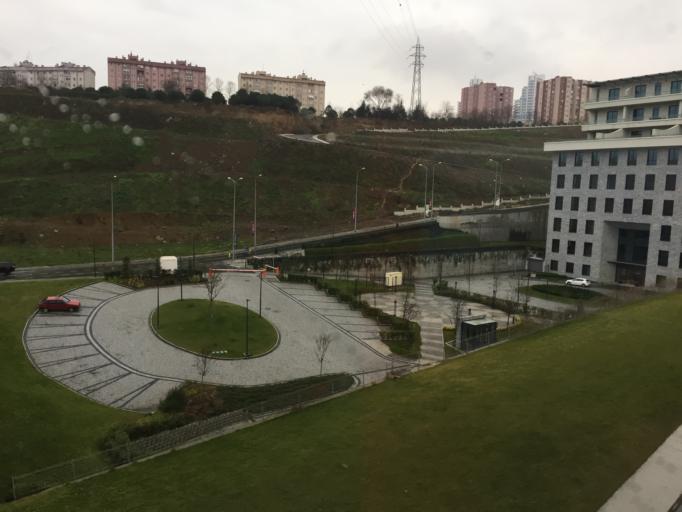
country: TR
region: Istanbul
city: Sisli
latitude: 41.1055
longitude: 28.9899
